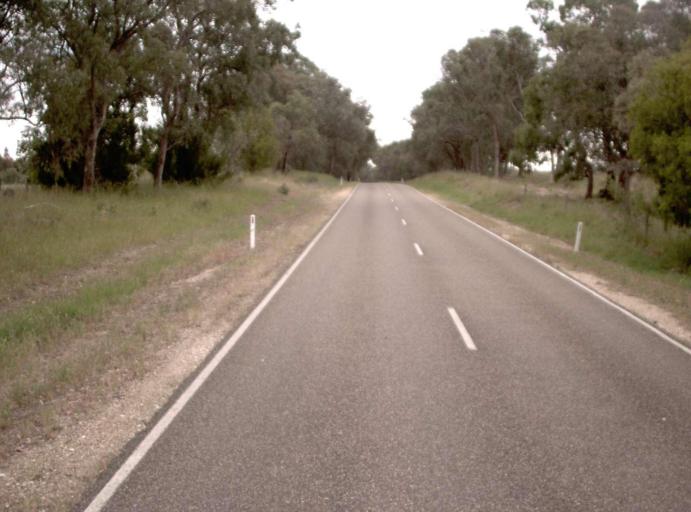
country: AU
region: Victoria
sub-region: East Gippsland
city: Bairnsdale
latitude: -37.7613
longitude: 147.3214
